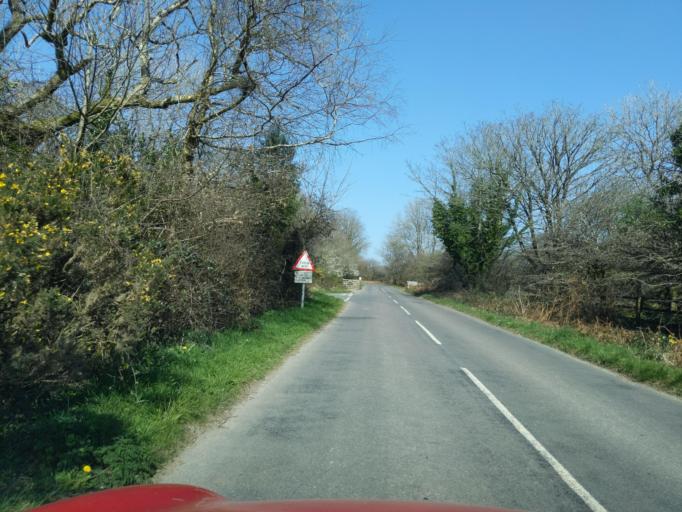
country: GB
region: England
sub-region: Devon
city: Horrabridge
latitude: 50.4916
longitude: -4.1088
